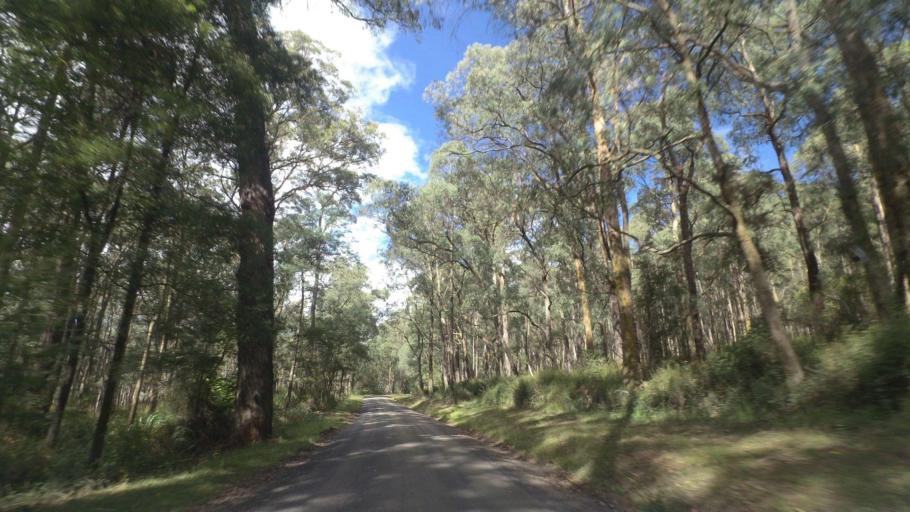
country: AU
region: Victoria
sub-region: Cardinia
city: Gembrook
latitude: -37.8847
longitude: 145.6193
